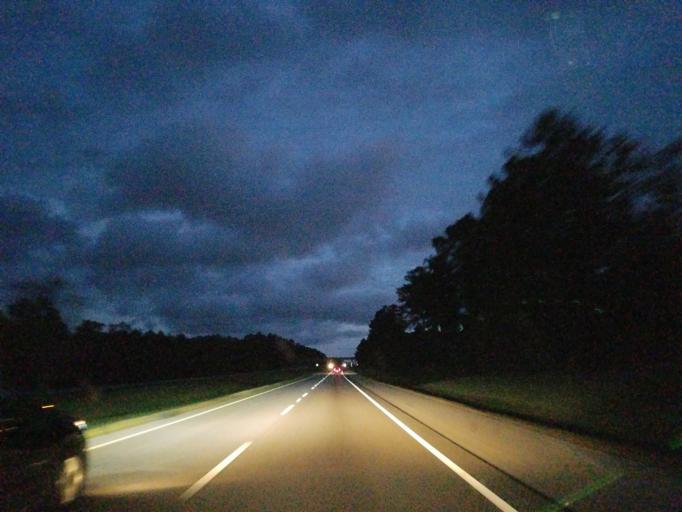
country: US
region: Mississippi
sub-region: Jones County
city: Sharon
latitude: 31.8418
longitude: -89.0496
